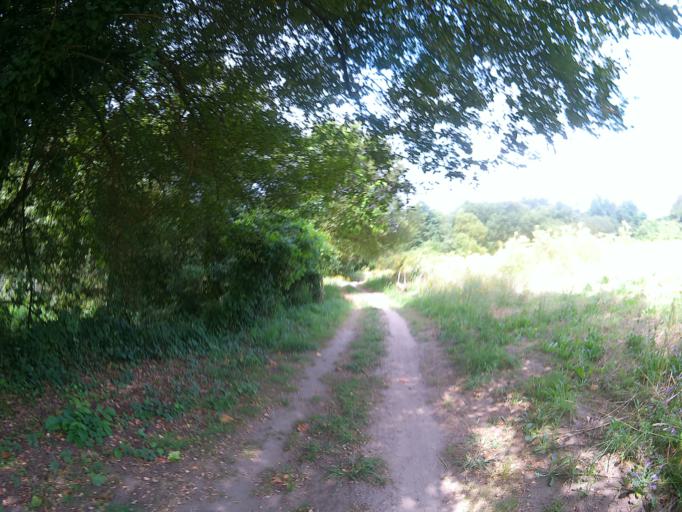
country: PT
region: Viana do Castelo
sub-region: Ponte de Lima
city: Ponte de Lima
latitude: 41.7811
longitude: -8.5461
